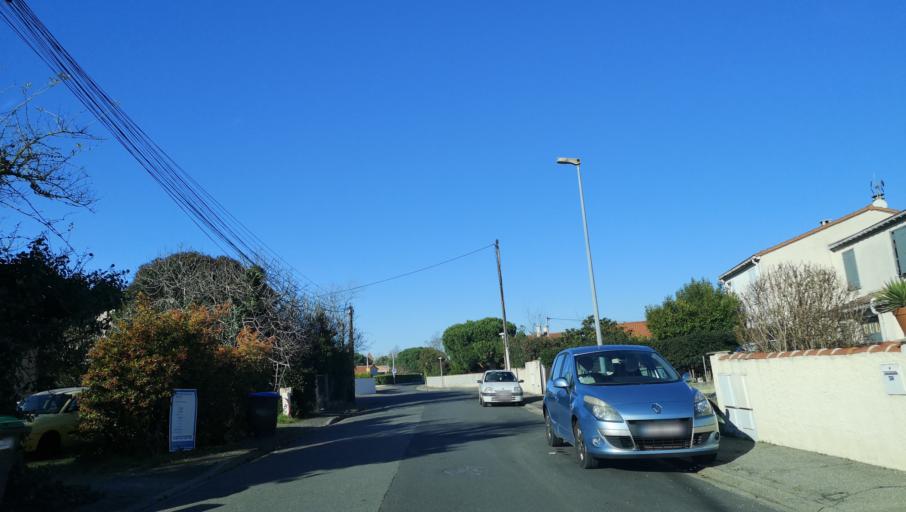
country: FR
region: Midi-Pyrenees
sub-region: Departement de la Haute-Garonne
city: Beauzelle
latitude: 43.6654
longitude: 1.3825
